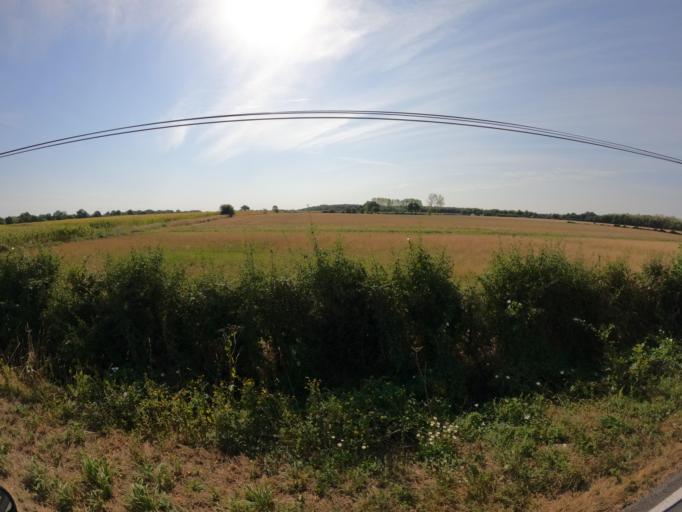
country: FR
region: Pays de la Loire
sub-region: Departement de la Vendee
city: Saint-Christophe-du-Ligneron
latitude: 46.8366
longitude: -1.7530
